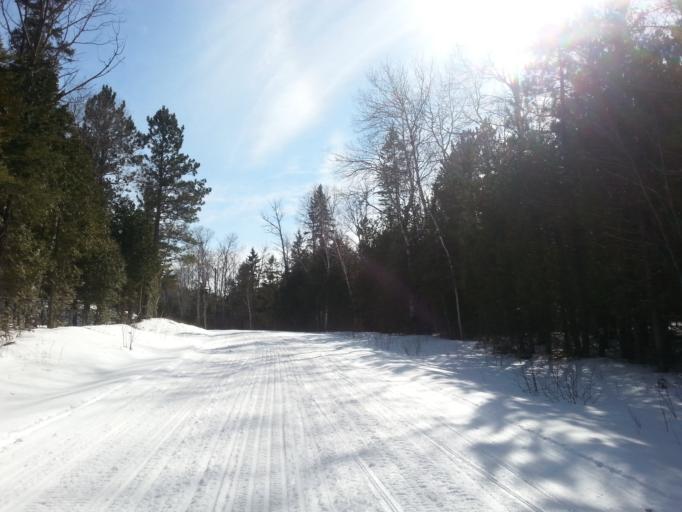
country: CA
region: Ontario
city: Greater Sudbury
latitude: 46.3352
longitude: -80.9055
